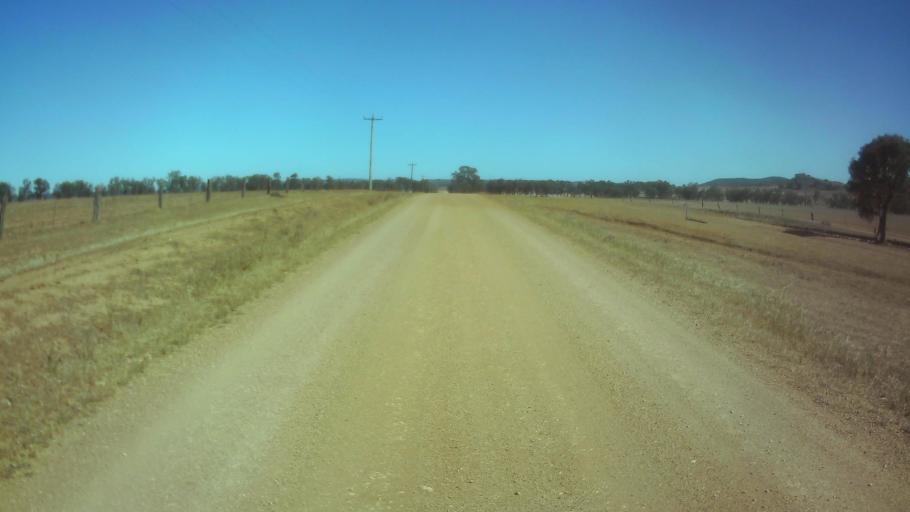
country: AU
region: New South Wales
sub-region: Weddin
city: Grenfell
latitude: -33.9507
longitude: 148.2985
